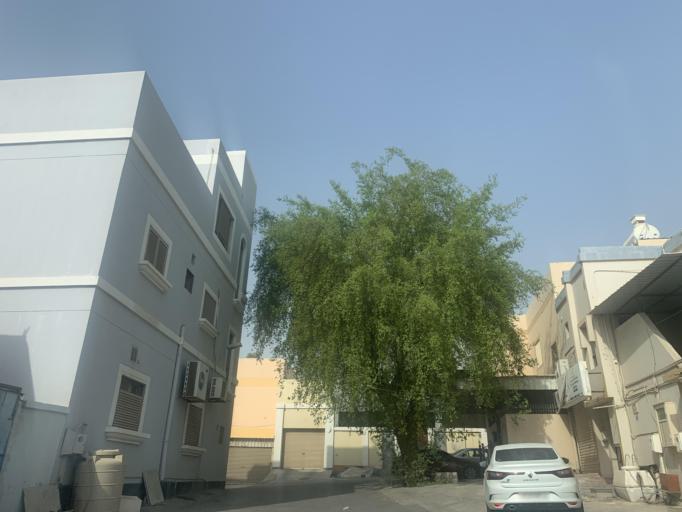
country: BH
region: Manama
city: Jidd Hafs
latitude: 26.2102
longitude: 50.4743
